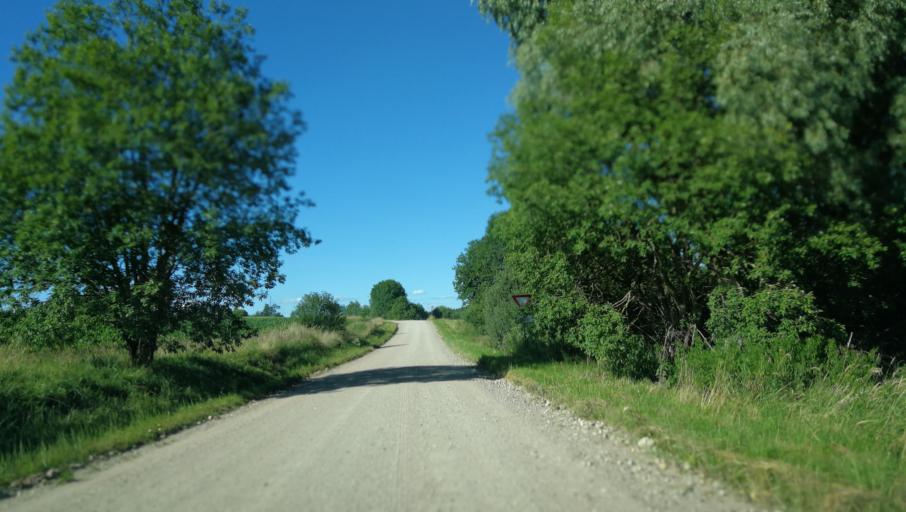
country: LV
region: Jaunpiebalga
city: Jaunpiebalga
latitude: 57.0155
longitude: 26.0517
